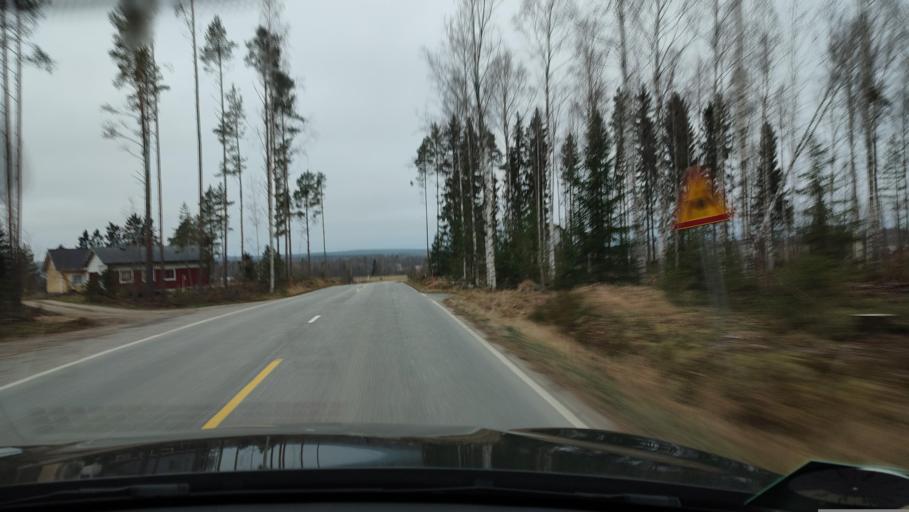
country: FI
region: Southern Ostrobothnia
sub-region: Suupohja
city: Karijoki
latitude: 62.2660
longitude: 21.7264
